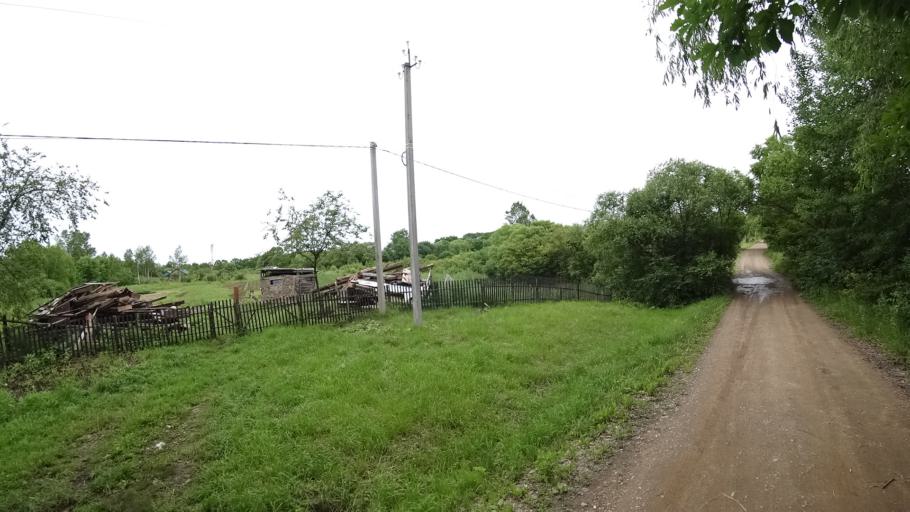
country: RU
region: Primorskiy
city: Arsen'yev
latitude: 44.1897
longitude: 133.3069
